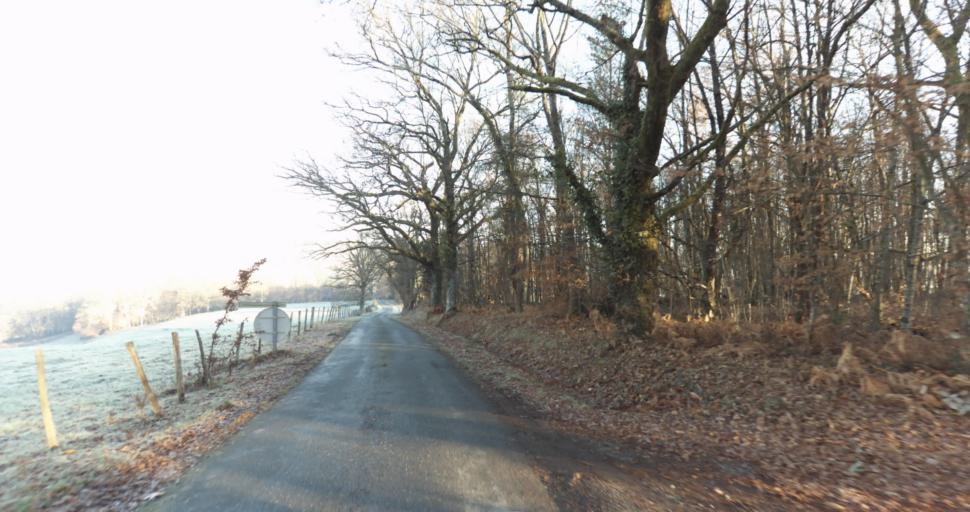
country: FR
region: Limousin
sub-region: Departement de la Haute-Vienne
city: Aixe-sur-Vienne
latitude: 45.8226
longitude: 1.1388
